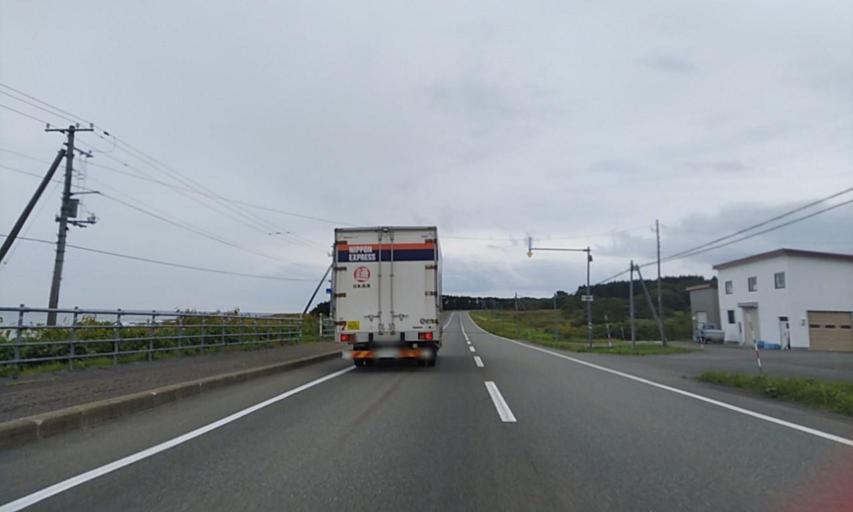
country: JP
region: Hokkaido
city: Nayoro
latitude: 45.0286
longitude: 142.5228
